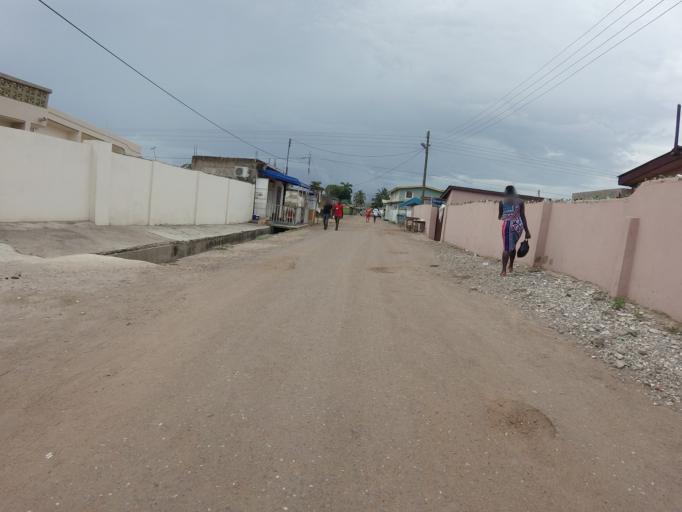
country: GH
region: Greater Accra
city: Accra
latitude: 5.5969
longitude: -0.2146
